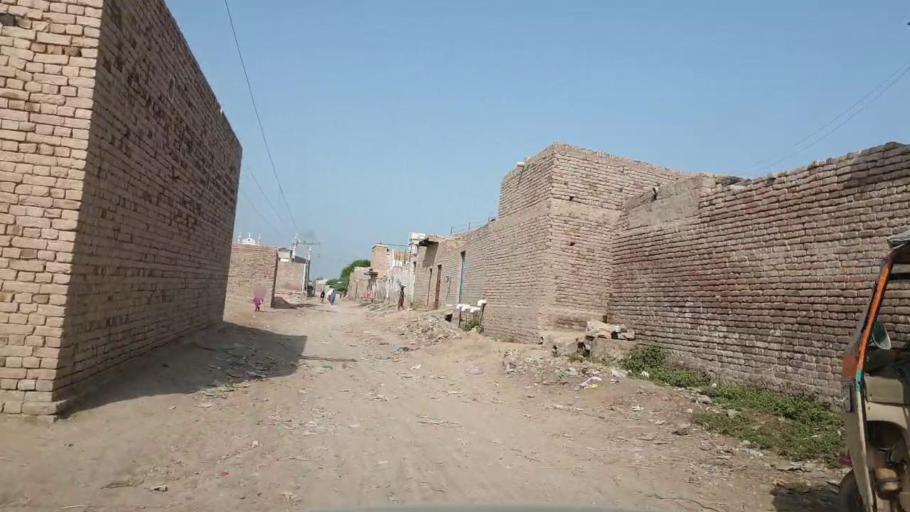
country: PK
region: Sindh
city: Bagarji
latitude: 27.8078
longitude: 68.7502
